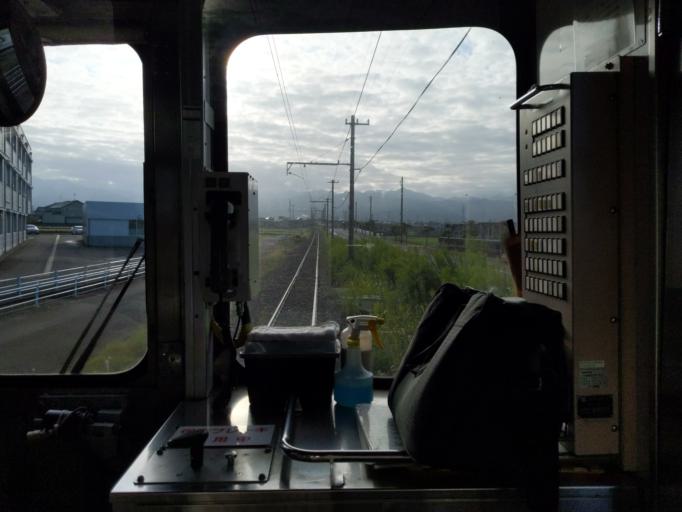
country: JP
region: Toyama
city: Kamiichi
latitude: 36.7046
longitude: 137.3090
